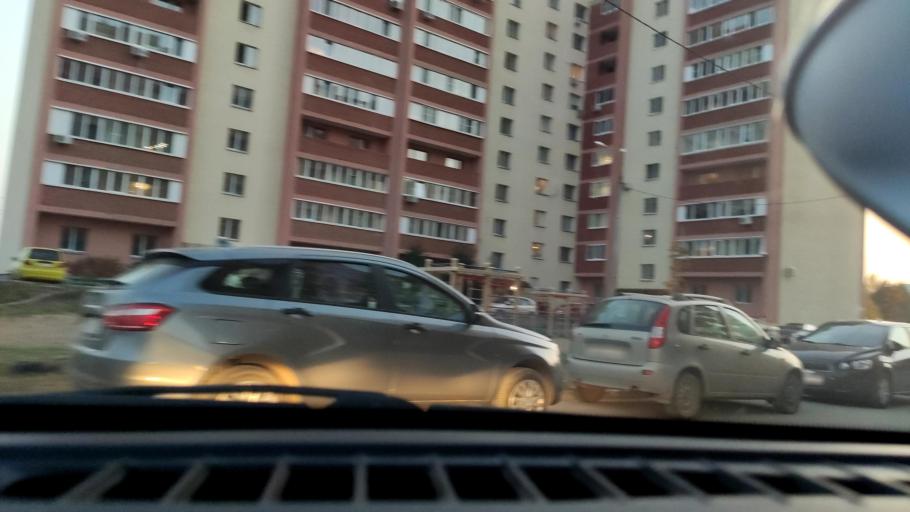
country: RU
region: Samara
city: Samara
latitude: 53.1493
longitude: 50.0905
